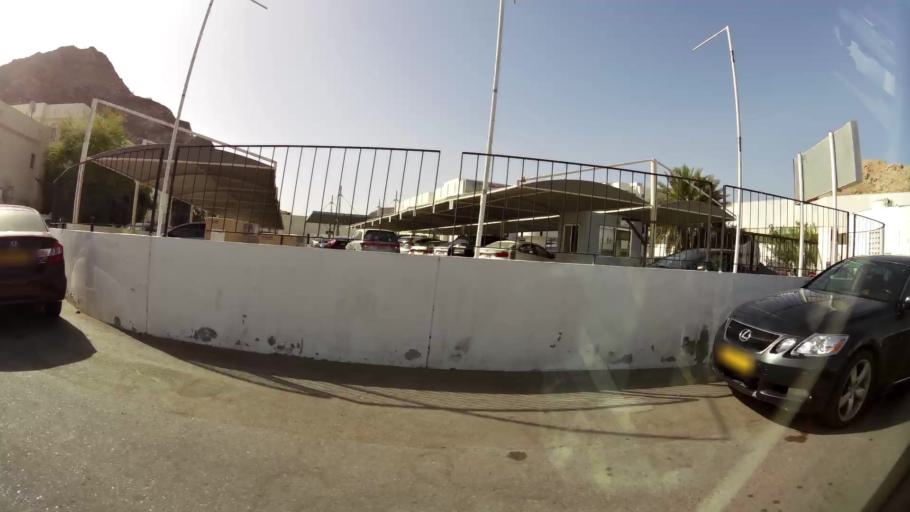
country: OM
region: Muhafazat Masqat
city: Muscat
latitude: 23.5964
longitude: 58.5185
